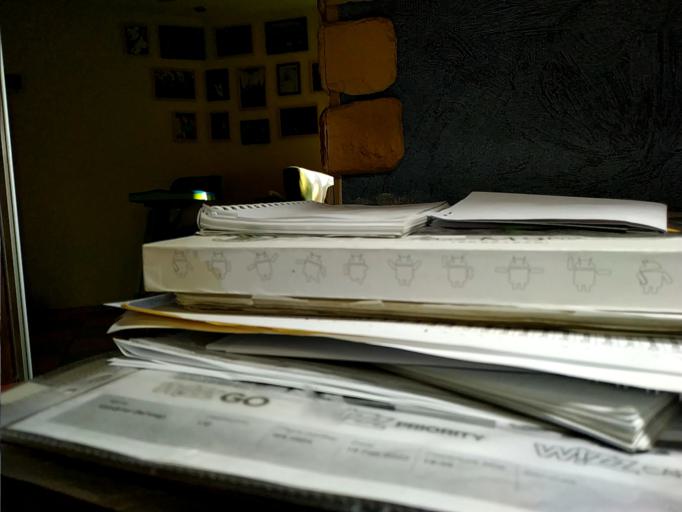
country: RU
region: Novgorod
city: Kholm
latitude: 57.1044
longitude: 31.4966
